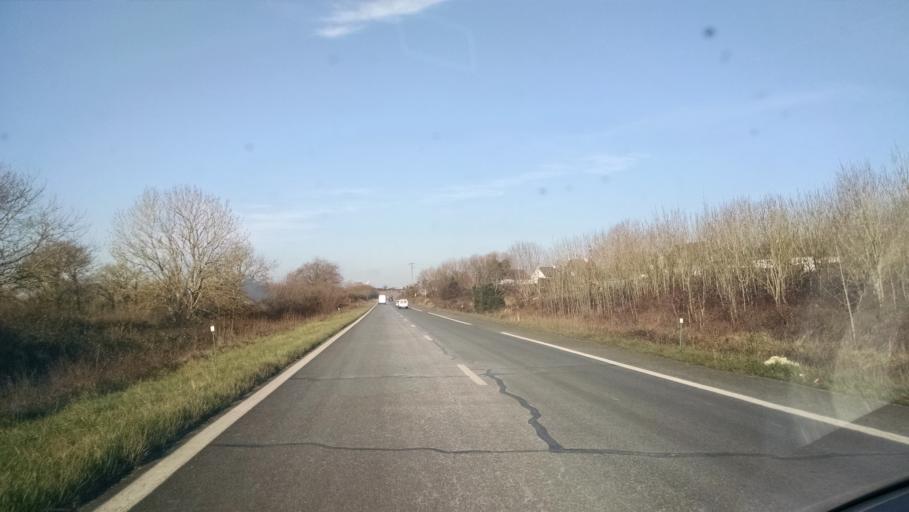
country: FR
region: Brittany
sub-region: Departement du Morbihan
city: Muzillac
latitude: 47.5634
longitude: -2.5077
